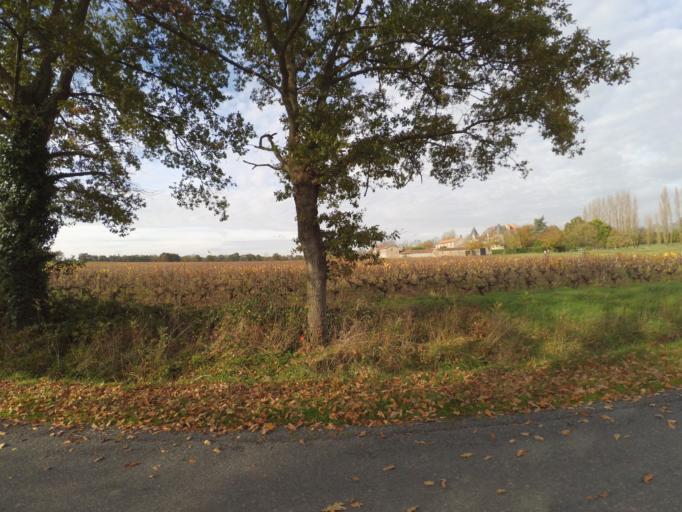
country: FR
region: Pays de la Loire
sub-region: Departement de la Vendee
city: Saint-Hilaire-de-Loulay
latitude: 47.0363
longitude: -1.3353
